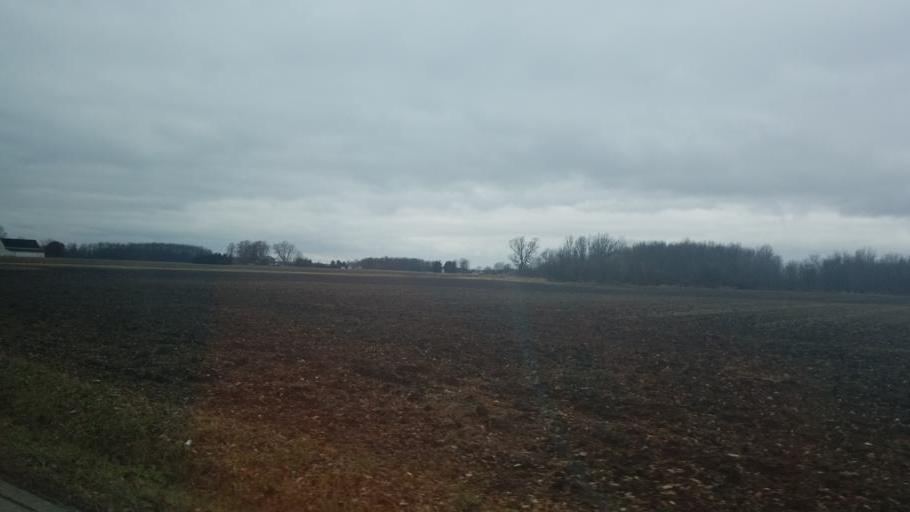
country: US
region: Ohio
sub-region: Crawford County
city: Crestline
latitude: 40.8145
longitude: -82.7239
